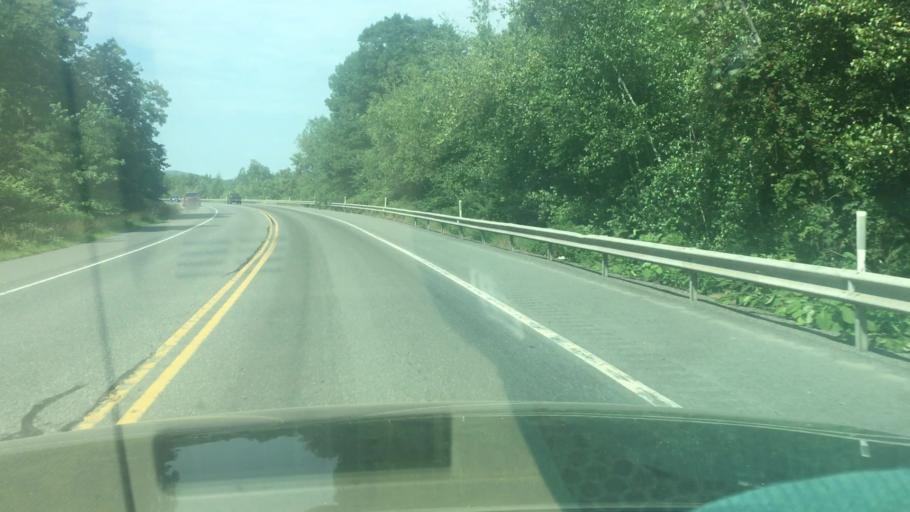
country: US
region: Pennsylvania
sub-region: Northumberland County
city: Kulpmont
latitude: 40.7908
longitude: -76.4428
